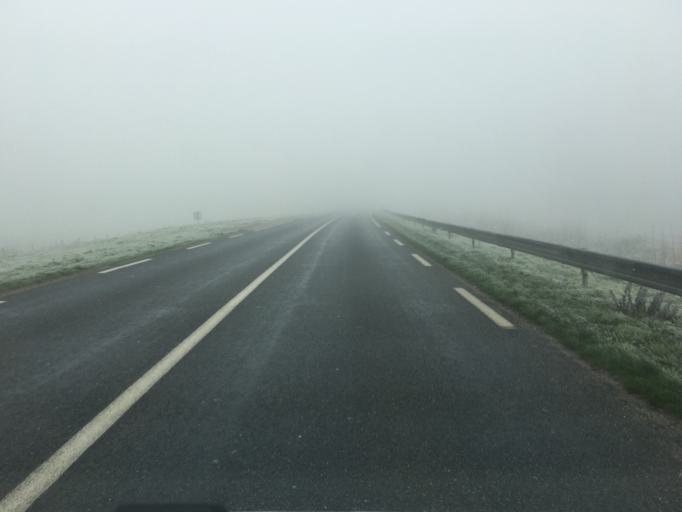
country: FR
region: Haute-Normandie
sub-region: Departement de la Seine-Maritime
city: Caudebec-en-Caux
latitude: 49.5079
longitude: 0.7407
